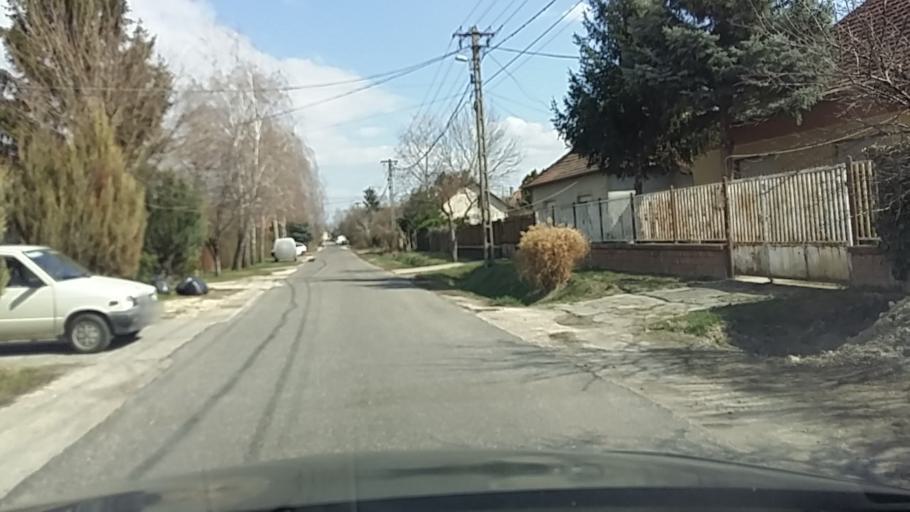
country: HU
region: Pest
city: Szigetszentmiklos
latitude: 47.3503
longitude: 19.0223
